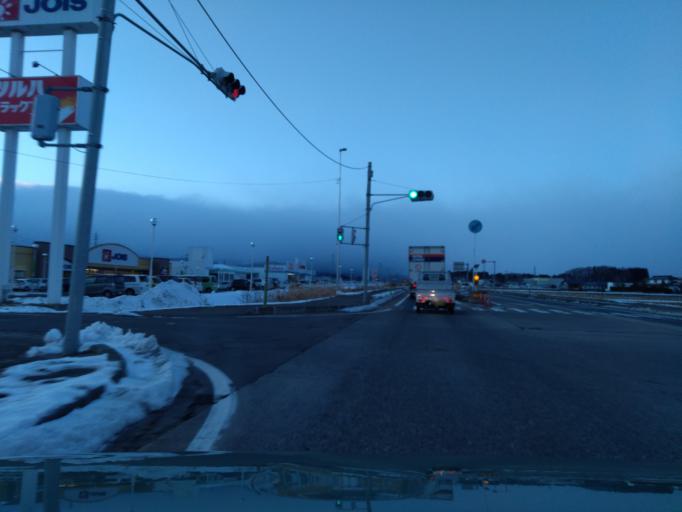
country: JP
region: Iwate
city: Shizukuishi
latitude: 39.6957
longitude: 140.9792
